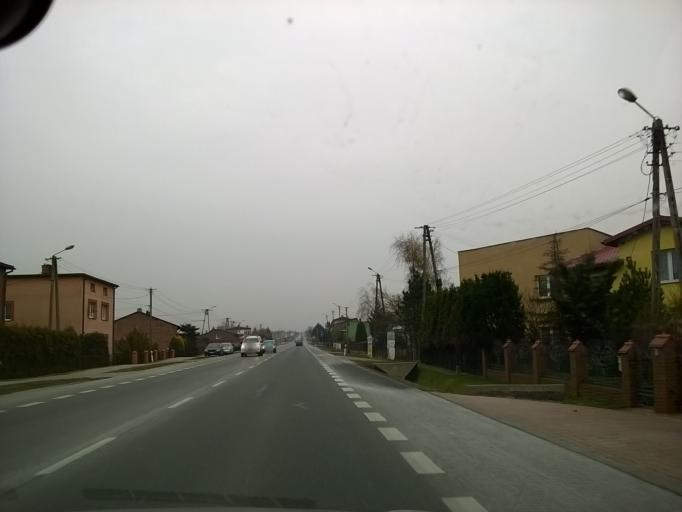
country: PL
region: Silesian Voivodeship
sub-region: Powiat gliwicki
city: Paniowki
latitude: 50.2412
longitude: 18.7648
